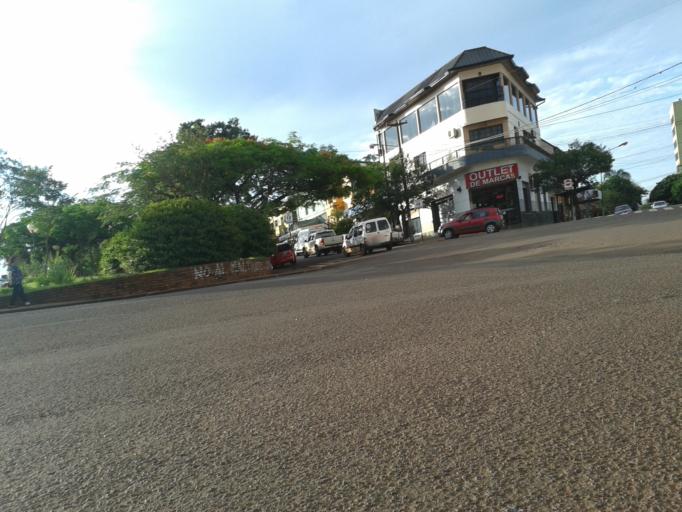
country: AR
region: Misiones
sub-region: Departamento de Obera
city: Obera
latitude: -27.4861
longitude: -55.1171
